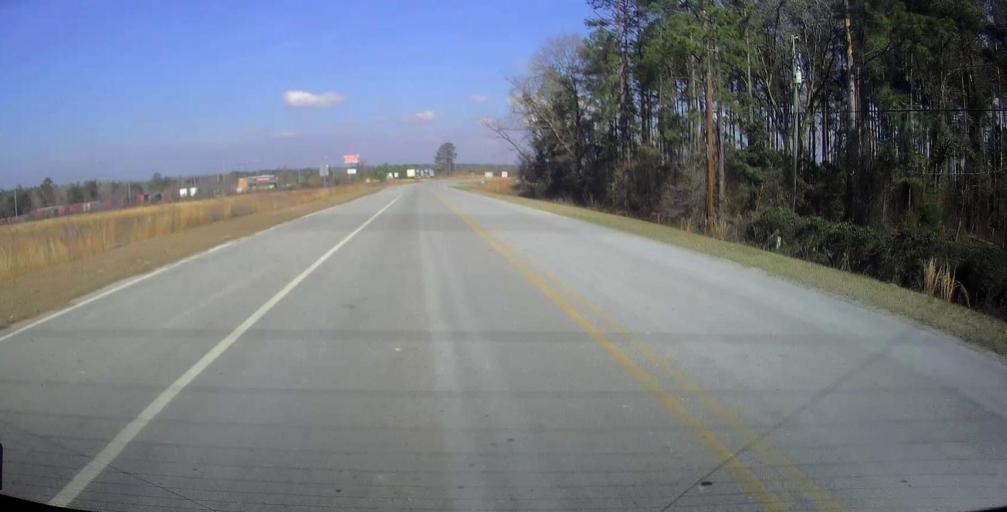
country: US
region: Georgia
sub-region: Wilkinson County
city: Gordon
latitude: 32.8947
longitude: -83.3077
